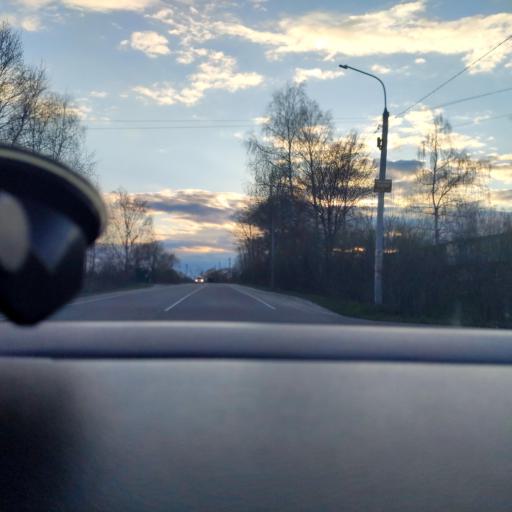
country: RU
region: Moskovskaya
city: Krasnyy Tkach
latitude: 55.4286
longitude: 39.2056
